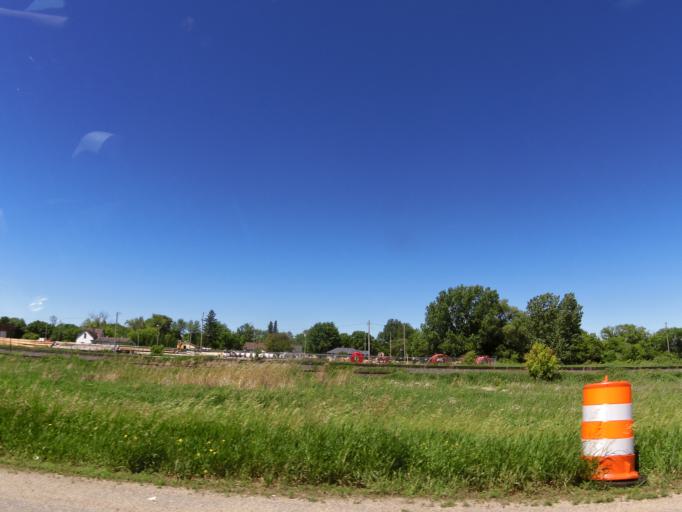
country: US
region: Minnesota
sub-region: Mahnomen County
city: Mahnomen
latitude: 47.3213
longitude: -95.9656
